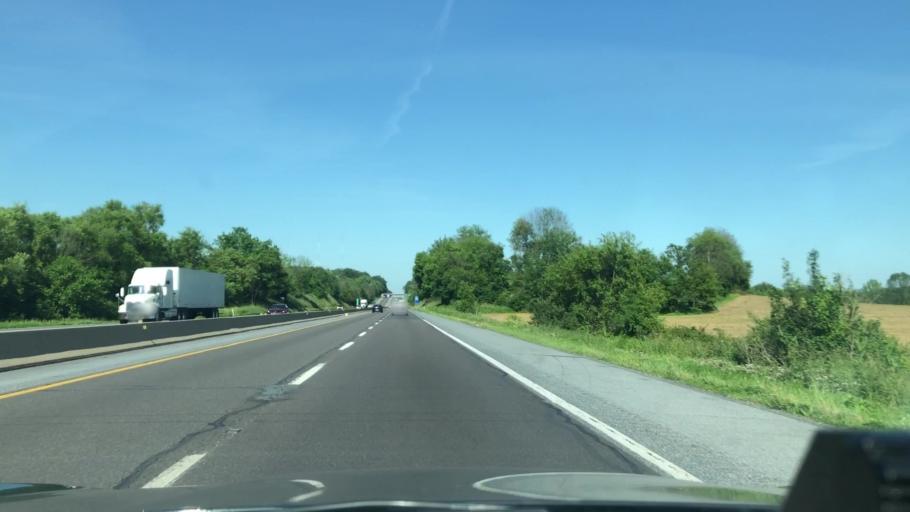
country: US
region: Pennsylvania
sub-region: Schuylkill County
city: Lake Wynonah
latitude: 40.5090
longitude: -76.1413
